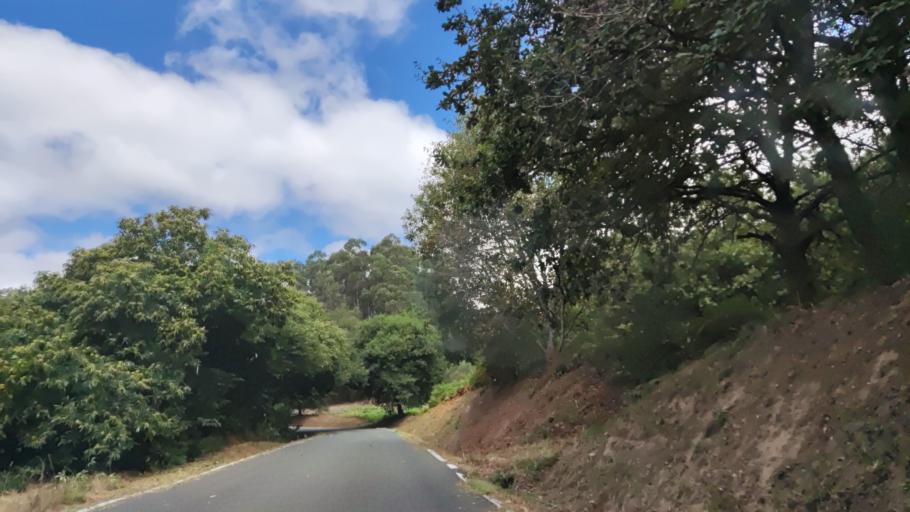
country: ES
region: Galicia
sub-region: Provincia da Coruna
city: Rois
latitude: 42.7470
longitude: -8.6994
